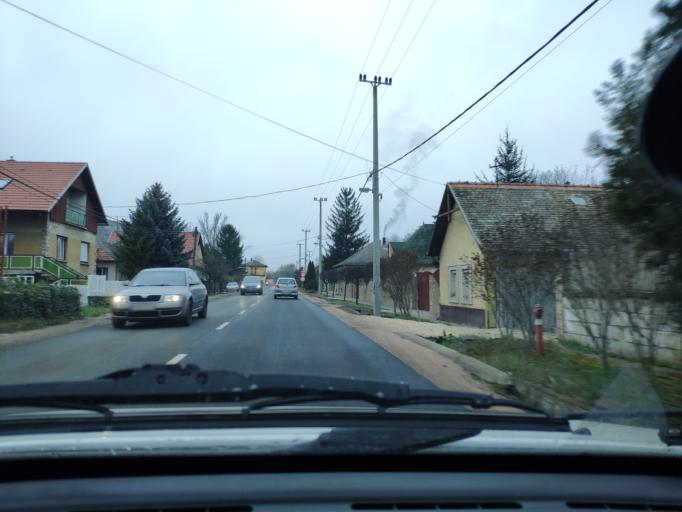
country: HU
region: Pest
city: Soskut
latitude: 47.4094
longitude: 18.8316
